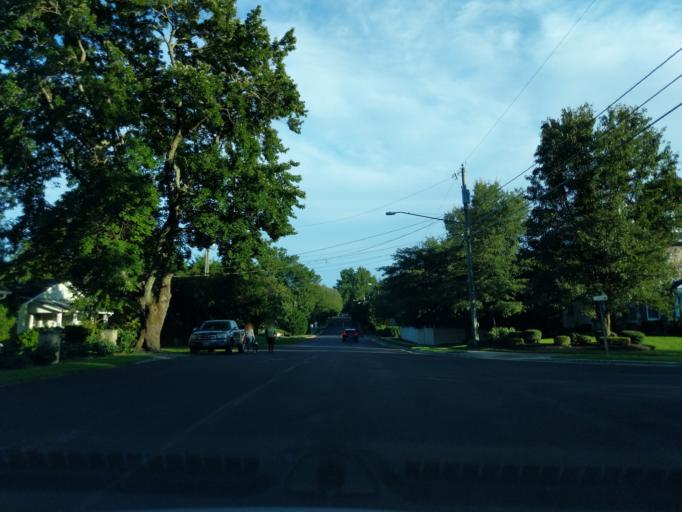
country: US
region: Virginia
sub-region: Fairfax County
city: Oakton
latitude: 38.8797
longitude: -77.2943
